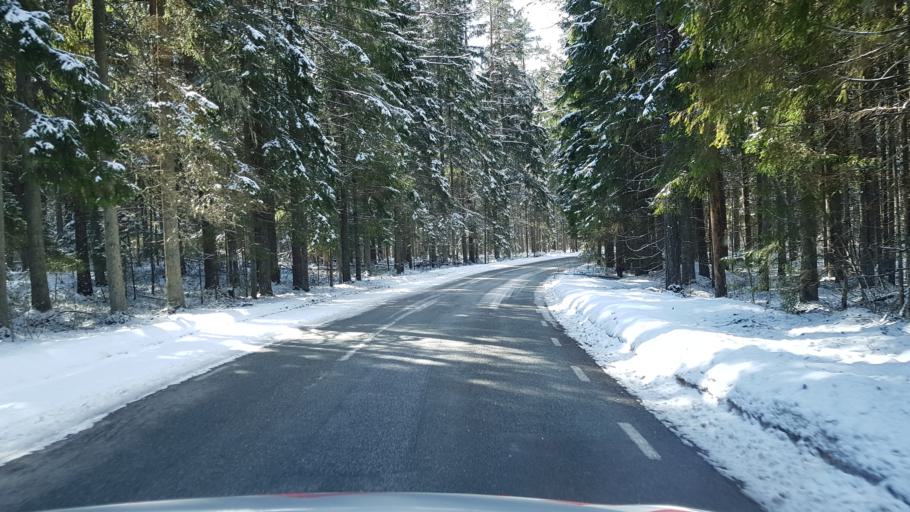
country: EE
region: Laeaene-Virumaa
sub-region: Kadrina vald
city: Kadrina
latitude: 59.5115
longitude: 25.9736
